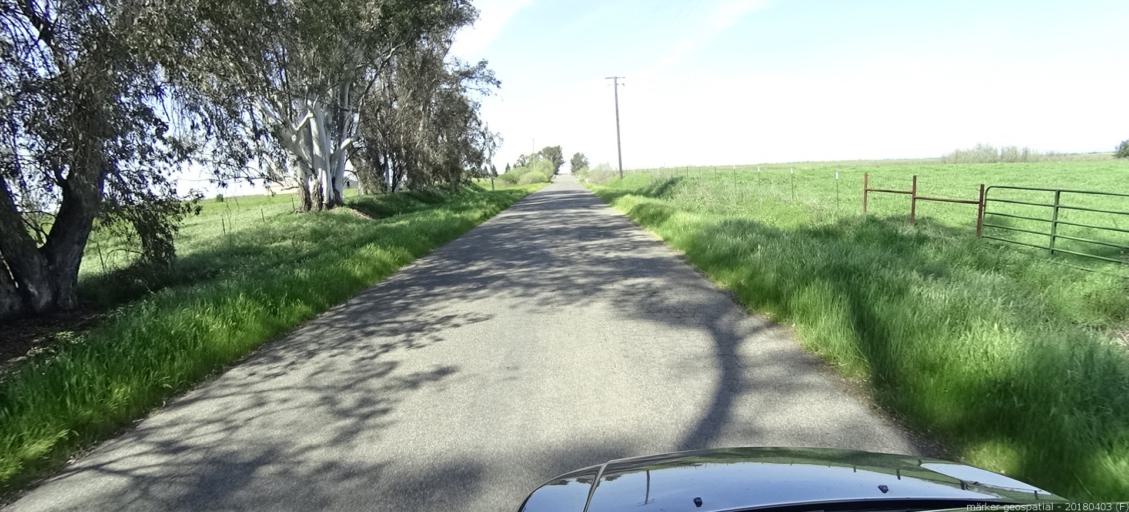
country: US
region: California
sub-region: Sacramento County
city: Herald
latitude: 38.3365
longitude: -121.2976
